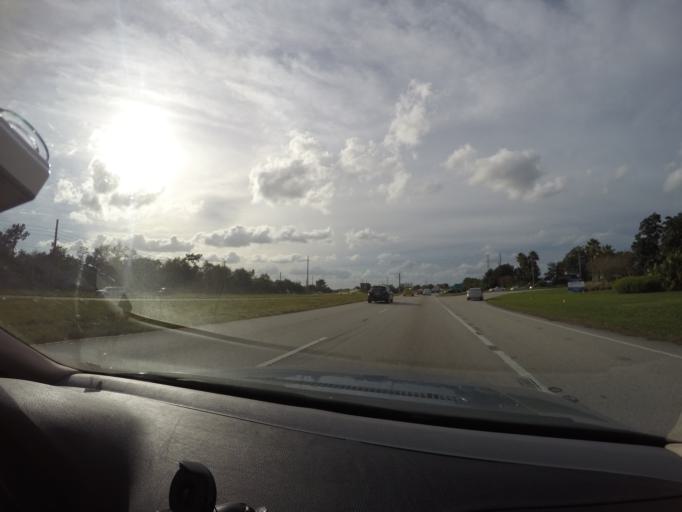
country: US
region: Florida
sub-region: Orange County
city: Tangelo Park
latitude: 28.4503
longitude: -81.4505
